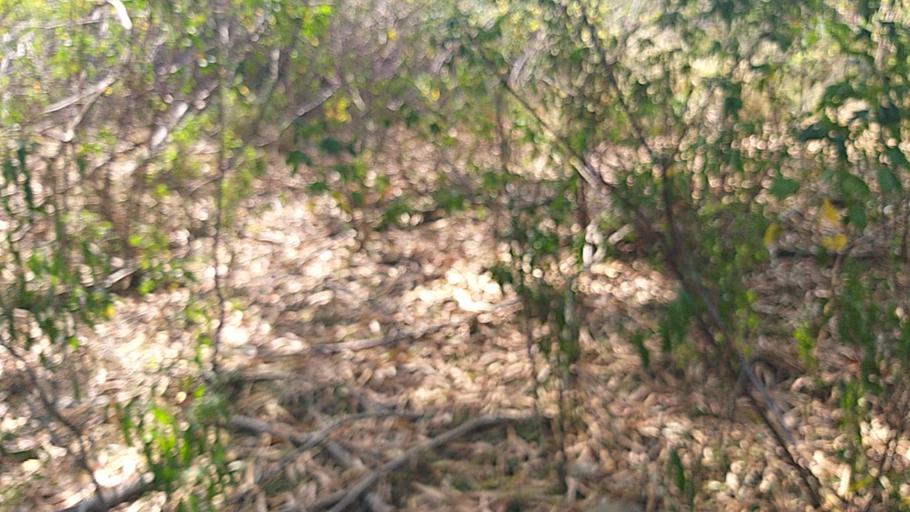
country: AU
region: New South Wales
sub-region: Wollongong
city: Mount Ousley
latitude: -34.4041
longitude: 150.8701
